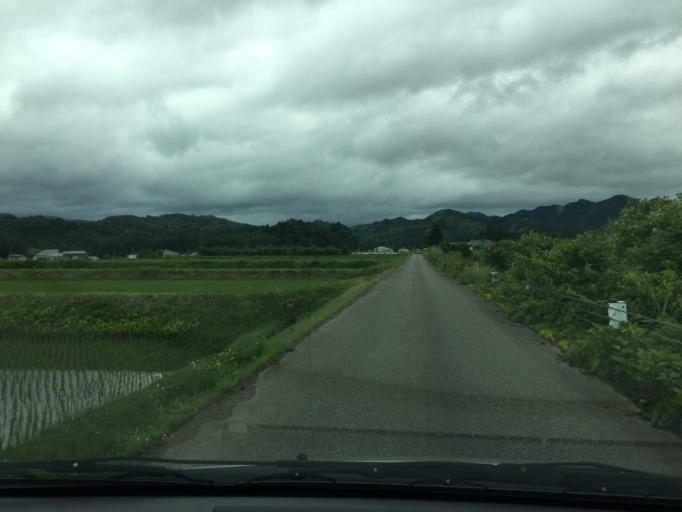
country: JP
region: Fukushima
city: Kitakata
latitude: 37.4399
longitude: 139.8169
